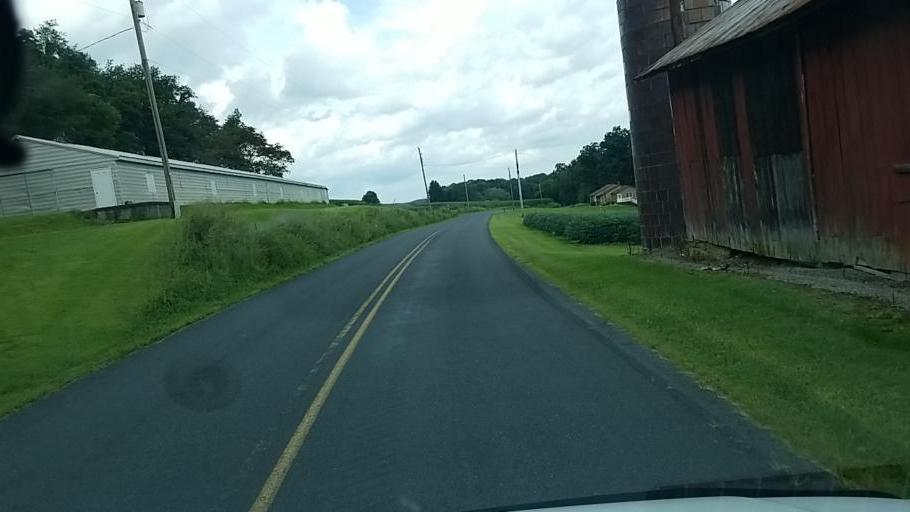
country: US
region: Pennsylvania
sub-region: Dauphin County
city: Elizabethville
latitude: 40.6534
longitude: -76.8480
